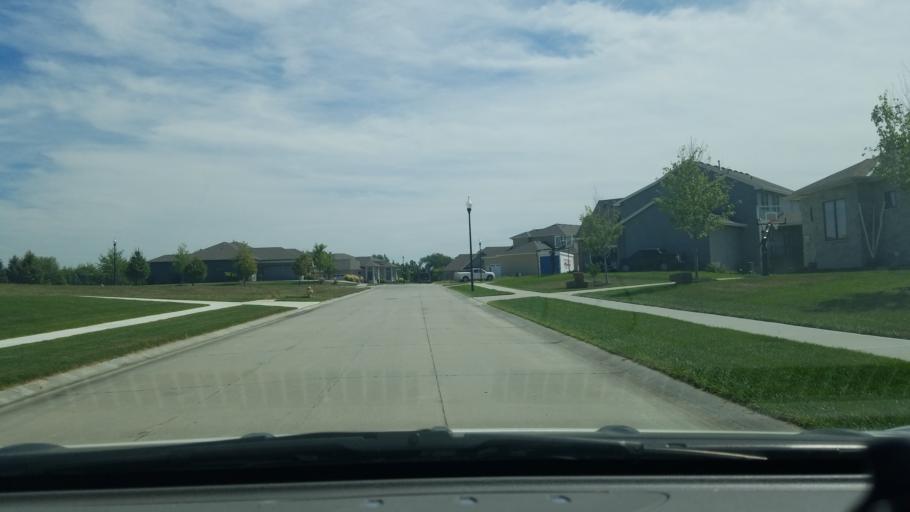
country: US
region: Nebraska
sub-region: Sarpy County
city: Papillion
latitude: 41.1432
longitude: -96.1032
